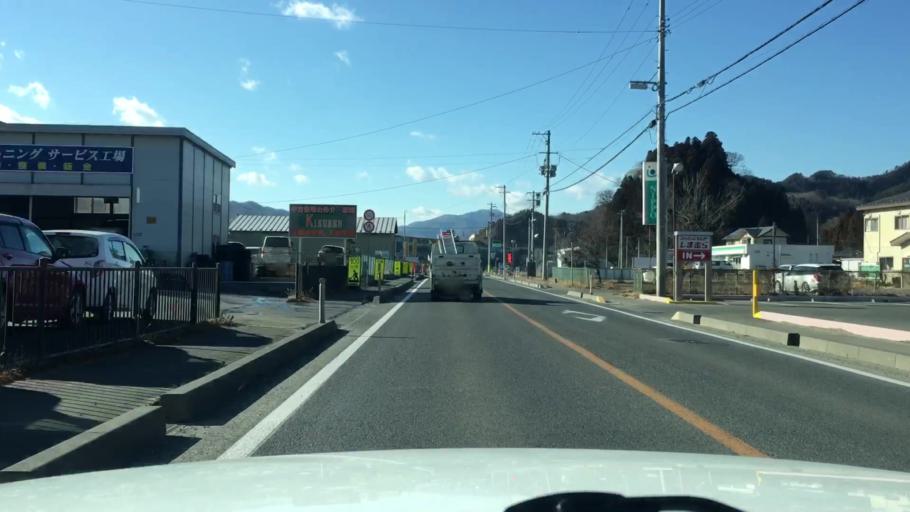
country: JP
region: Iwate
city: Miyako
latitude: 39.6322
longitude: 141.8935
